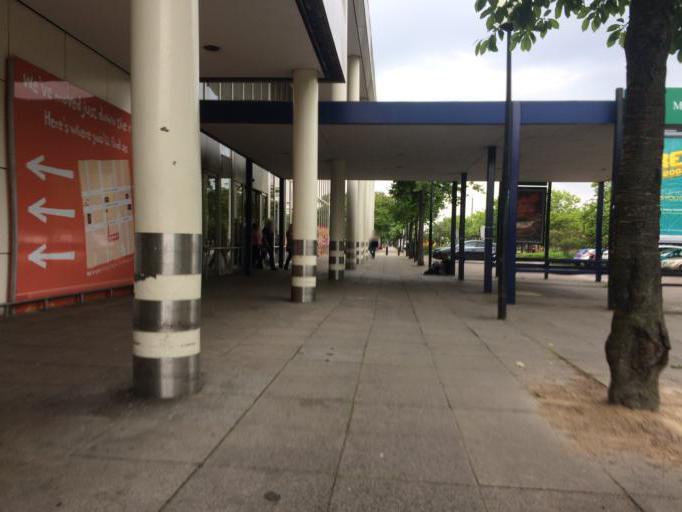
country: GB
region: England
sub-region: Milton Keynes
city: Milton Keynes
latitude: 52.0425
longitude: -0.7506
